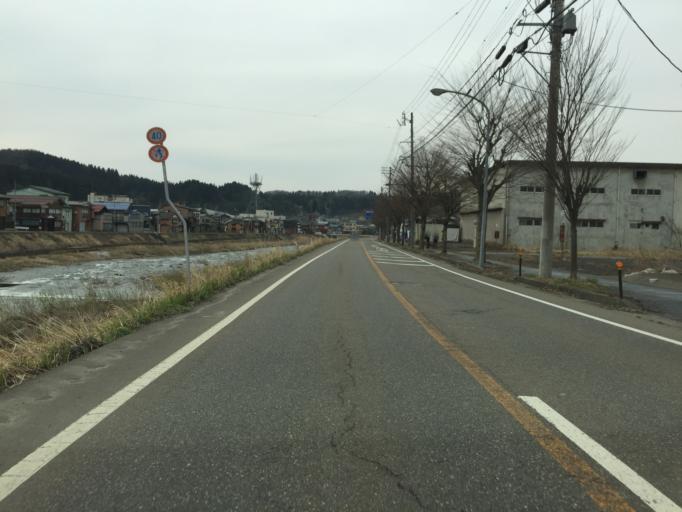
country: JP
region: Niigata
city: Tochio-honcho
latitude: 37.4757
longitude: 138.9995
